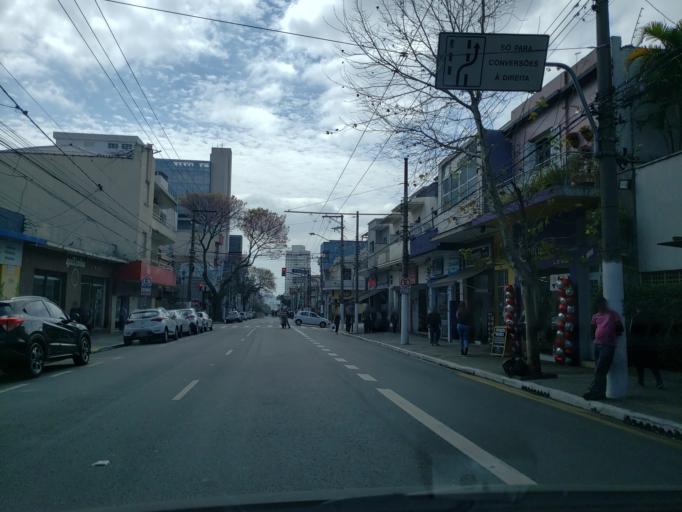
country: BR
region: Sao Paulo
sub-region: Sao Paulo
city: Sao Paulo
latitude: -23.5757
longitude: -46.6234
